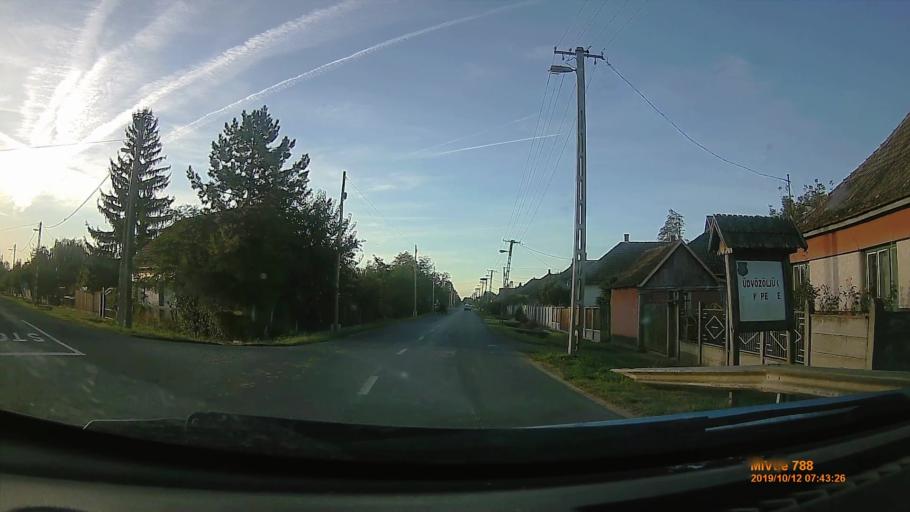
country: RO
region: Bihor
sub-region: Comuna Bors
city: Bors
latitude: 47.1935
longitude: 21.7876
